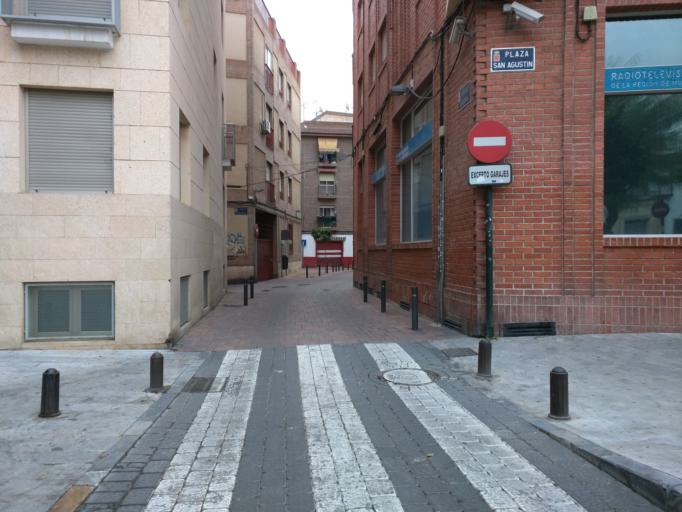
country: ES
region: Murcia
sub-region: Murcia
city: Murcia
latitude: 37.9870
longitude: -1.1379
